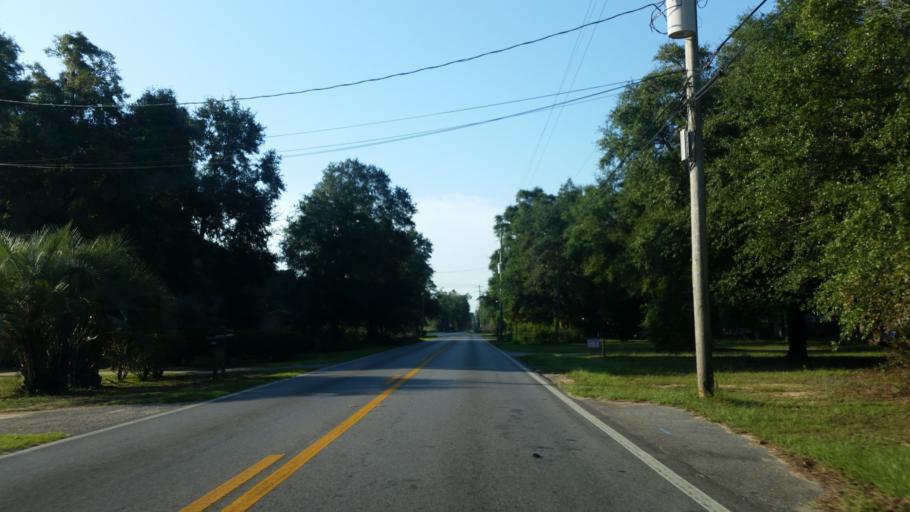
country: US
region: Florida
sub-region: Santa Rosa County
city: Bagdad
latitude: 30.5893
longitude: -87.0653
